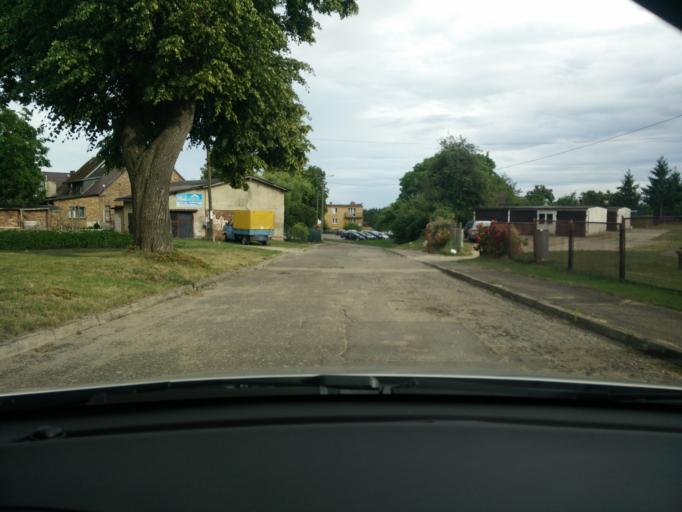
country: PL
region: Pomeranian Voivodeship
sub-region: Powiat pucki
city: Mrzezino
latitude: 54.6687
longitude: 18.4551
